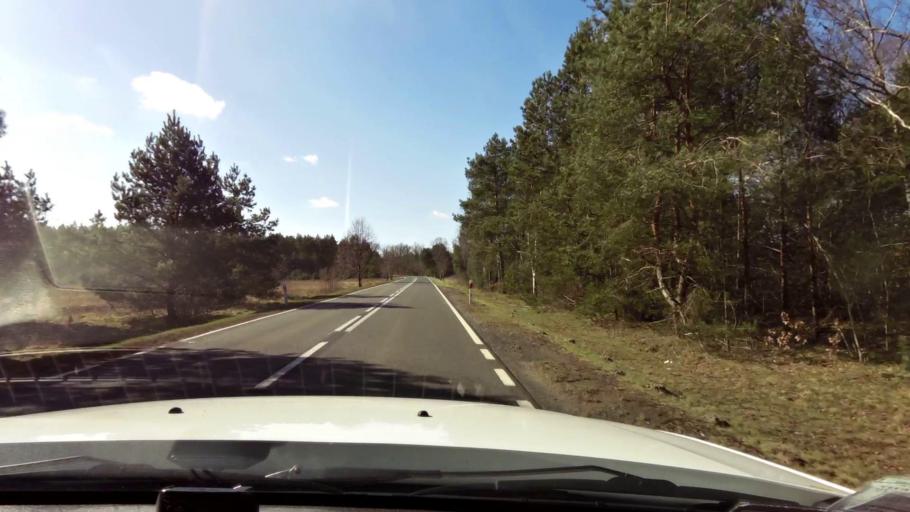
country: PL
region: West Pomeranian Voivodeship
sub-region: Powiat gryfinski
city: Gryfino
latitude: 53.2119
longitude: 14.4821
